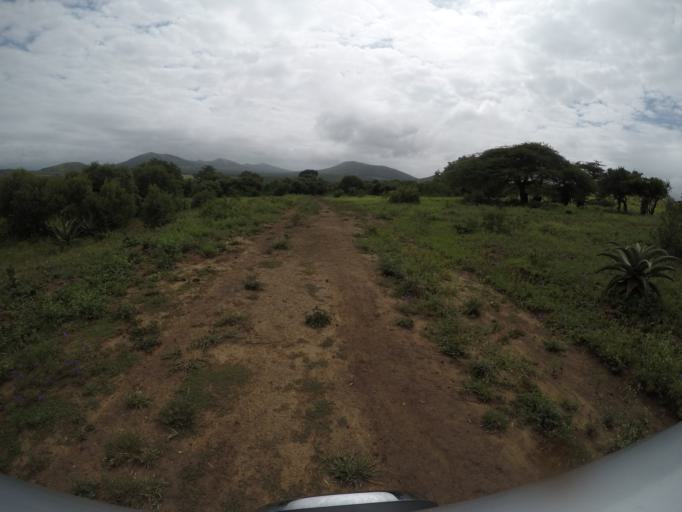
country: ZA
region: KwaZulu-Natal
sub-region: uThungulu District Municipality
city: Empangeni
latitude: -28.6253
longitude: 31.8635
